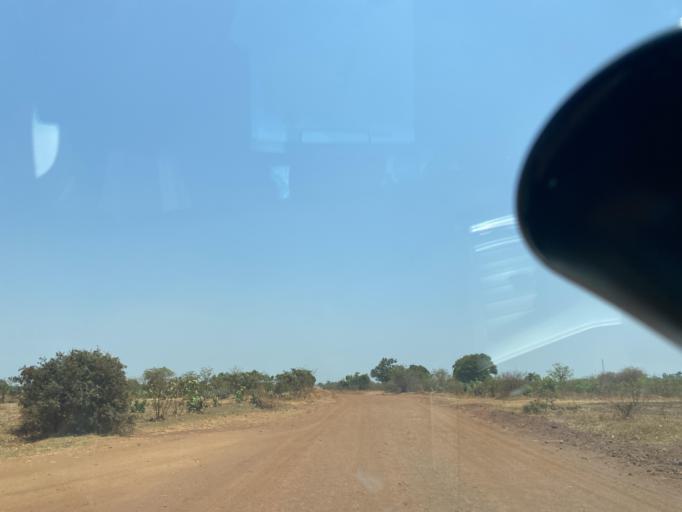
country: ZM
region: Southern
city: Nakambala
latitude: -15.5030
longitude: 27.9173
